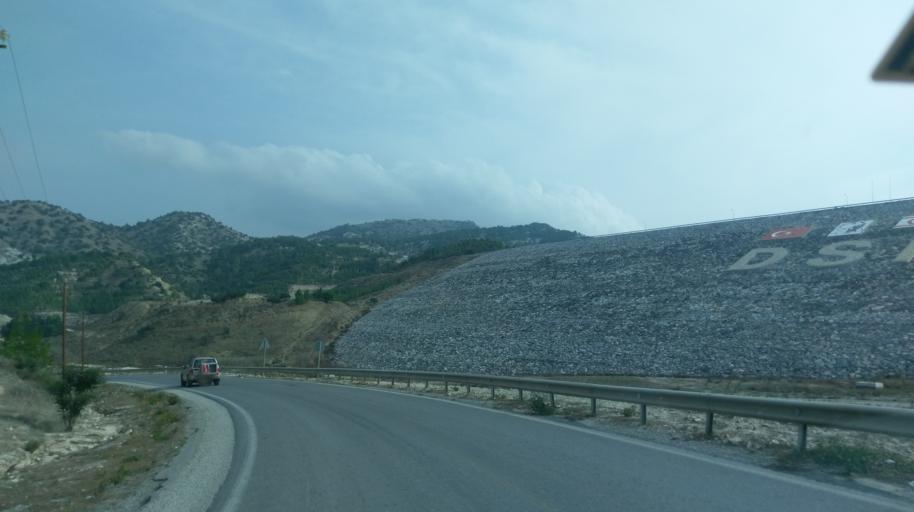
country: CY
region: Keryneia
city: Lapithos
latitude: 35.3302
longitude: 33.0682
